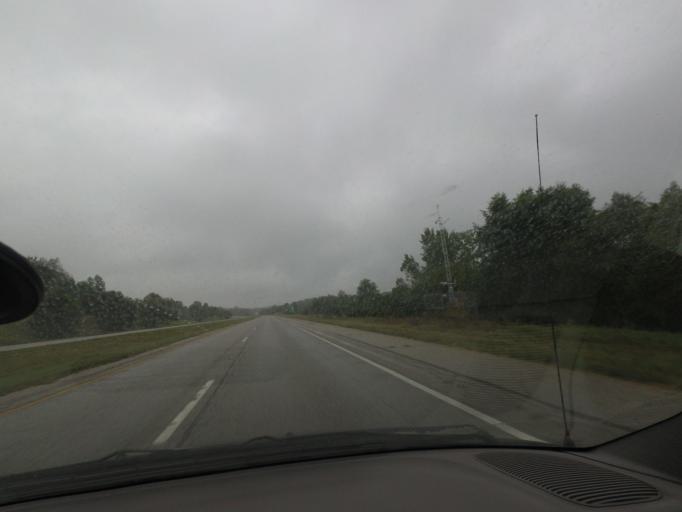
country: US
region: Illinois
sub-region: Pike County
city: Barry
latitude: 39.7140
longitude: -91.0628
